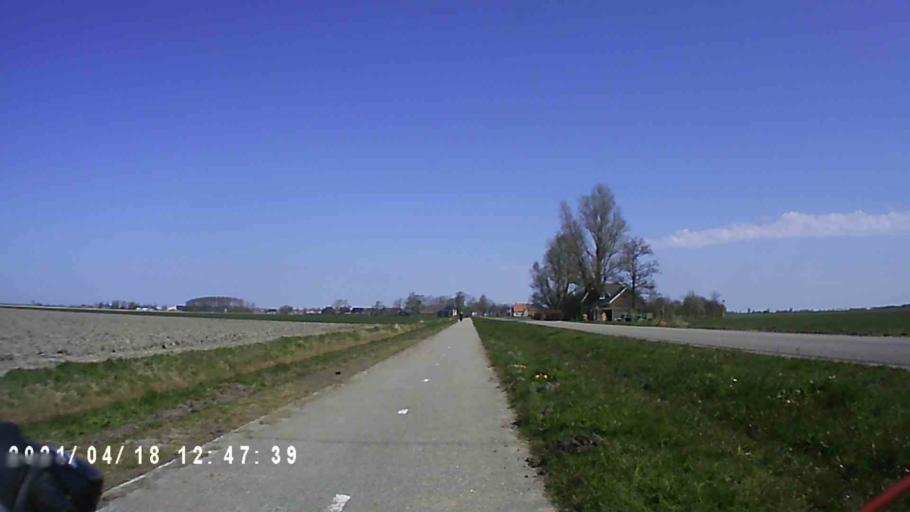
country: NL
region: Friesland
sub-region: Gemeente Dongeradeel
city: Dokkum
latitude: 53.3708
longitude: 6.0500
